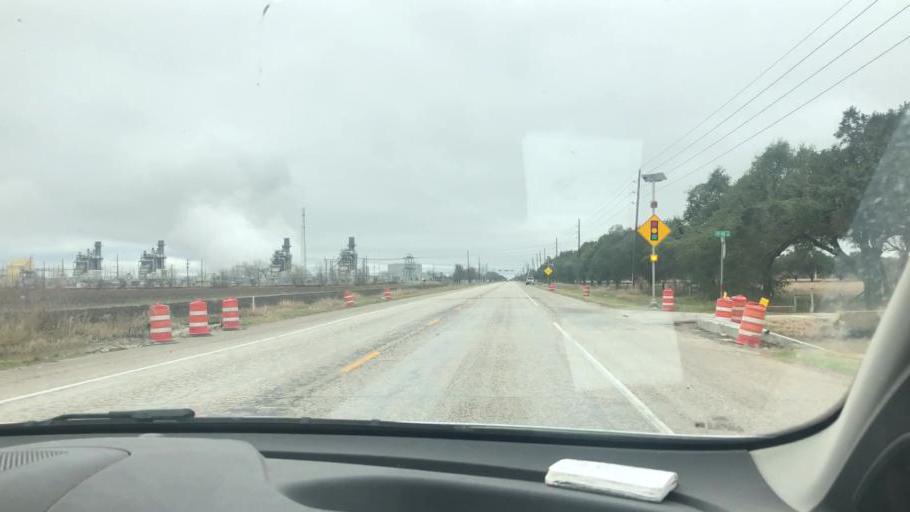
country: US
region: Texas
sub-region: Wharton County
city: Wharton
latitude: 29.2925
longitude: -96.0732
